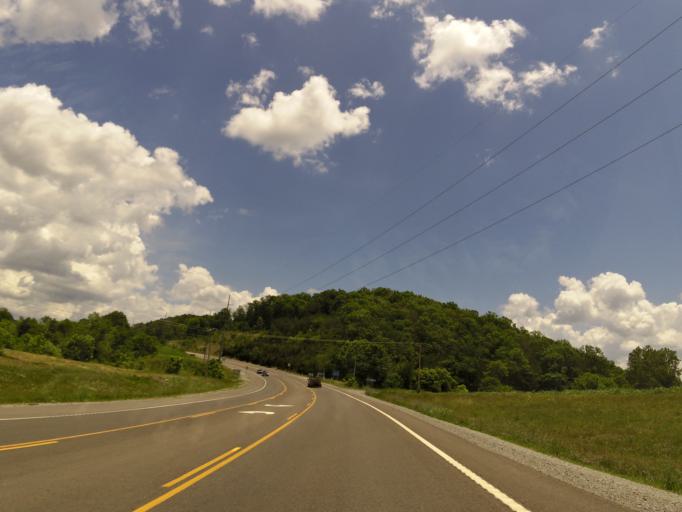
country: US
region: Tennessee
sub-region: Claiborne County
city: New Tazewell
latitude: 36.3958
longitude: -83.6832
